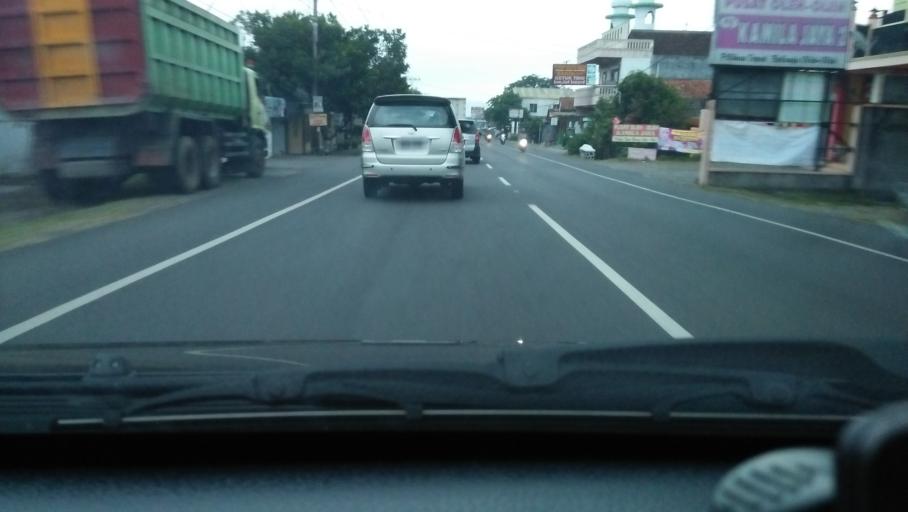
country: ID
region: Central Java
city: Magelang
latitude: -7.4194
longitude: 110.2334
